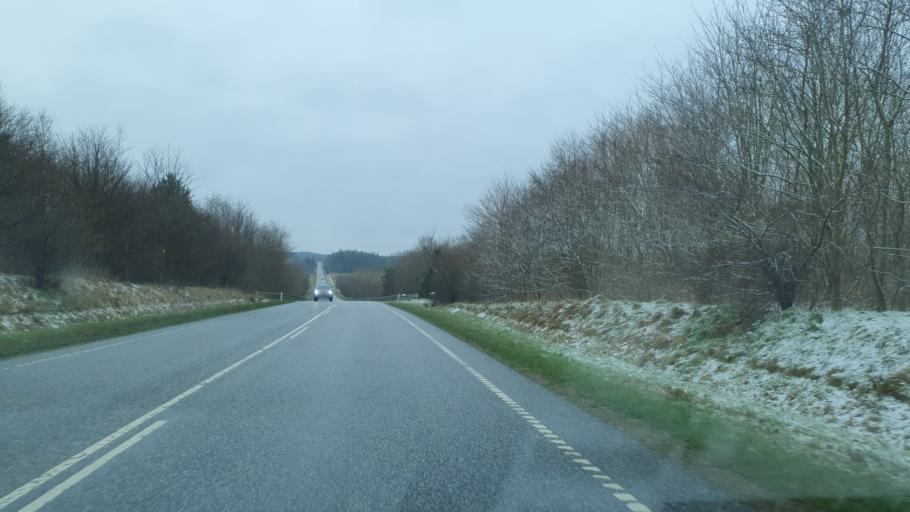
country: DK
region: North Denmark
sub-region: Jammerbugt Kommune
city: Brovst
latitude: 57.0932
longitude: 9.4549
